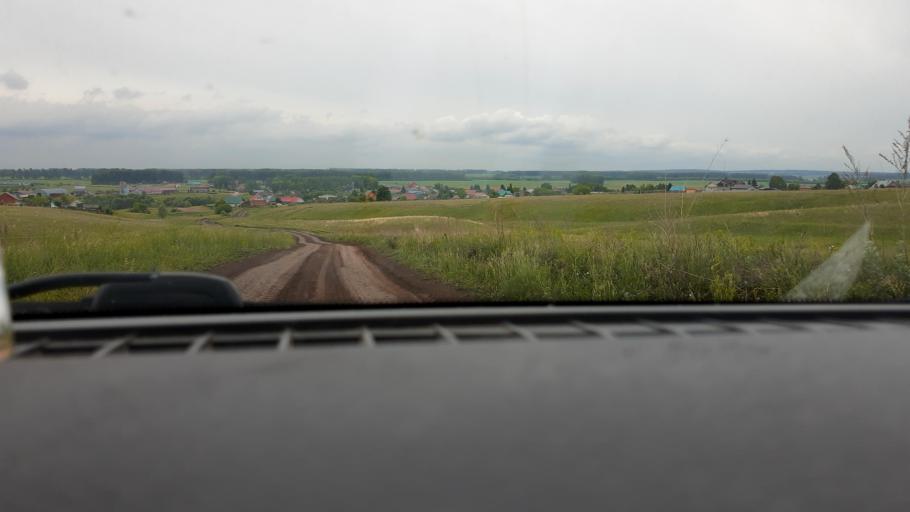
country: RU
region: Bashkortostan
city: Chishmy
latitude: 54.6890
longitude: 55.4844
